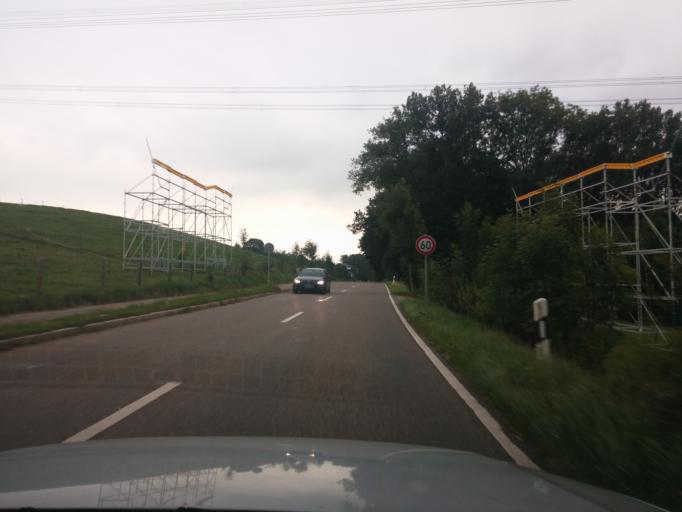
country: DE
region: Bavaria
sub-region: Swabia
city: Buxheim
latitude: 47.9882
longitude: 10.1405
